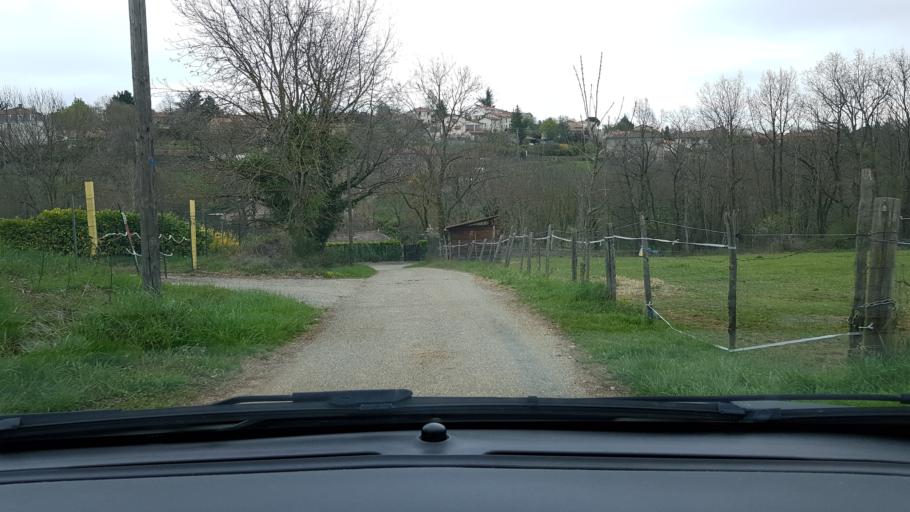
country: FR
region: Rhone-Alpes
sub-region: Departement du Rhone
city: Mornant
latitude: 45.6238
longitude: 4.6600
